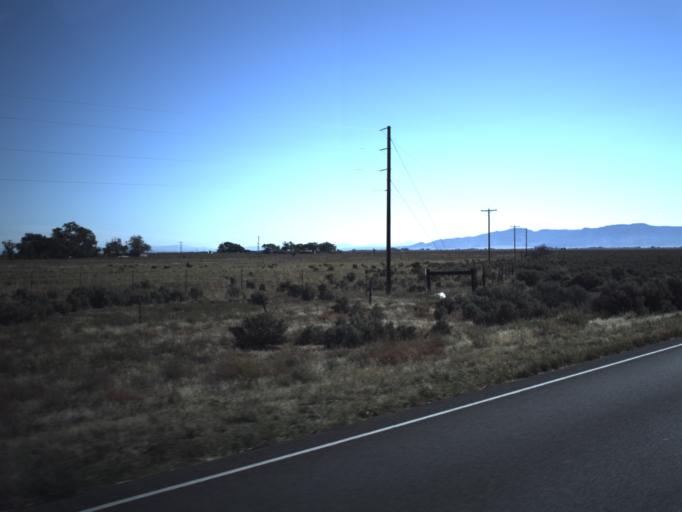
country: US
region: Utah
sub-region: Washington County
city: Enterprise
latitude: 37.7438
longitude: -113.7518
